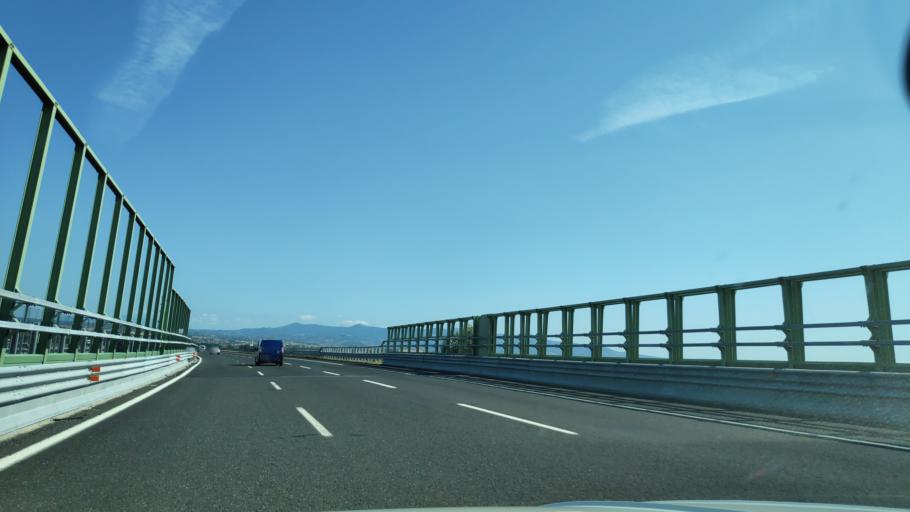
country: IT
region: Latium
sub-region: Citta metropolitana di Roma Capitale
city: Albuccione
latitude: 41.9517
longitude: 12.7026
